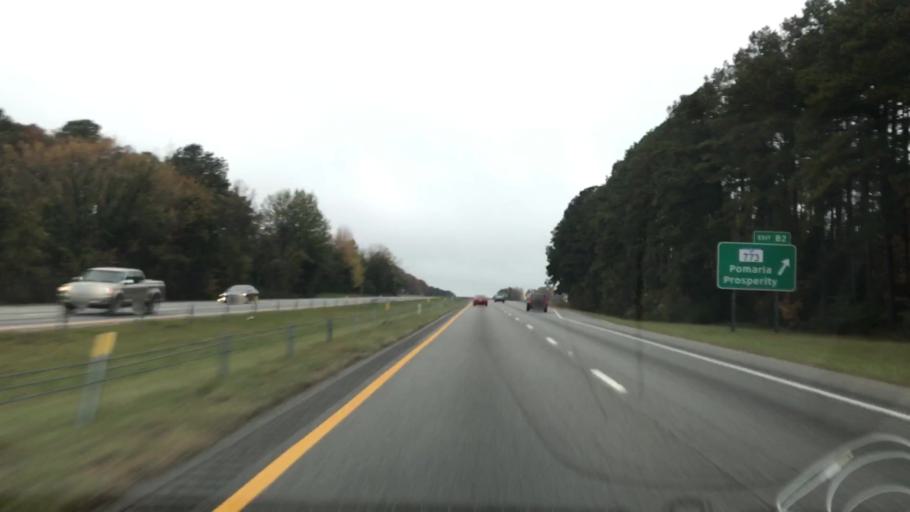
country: US
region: South Carolina
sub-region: Newberry County
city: Prosperity
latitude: 34.2370
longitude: -81.4545
